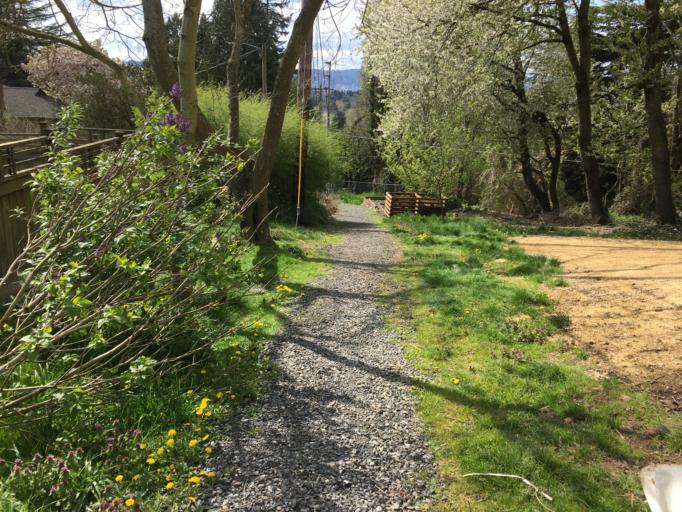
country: US
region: Oregon
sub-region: Multnomah County
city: Lents
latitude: 45.5192
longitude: -122.5978
